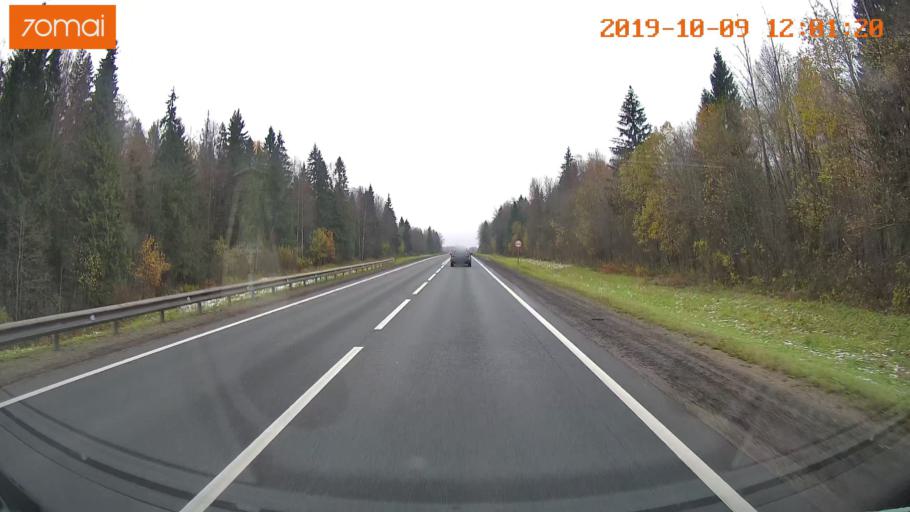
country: RU
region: Vologda
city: Gryazovets
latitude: 58.6891
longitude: 40.3030
